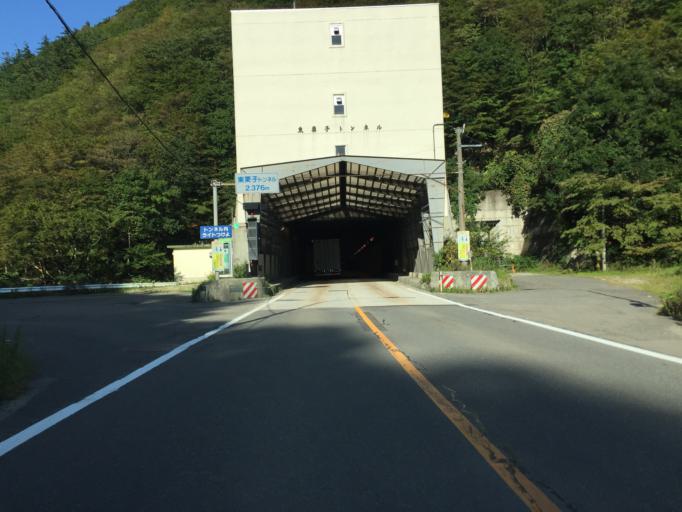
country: JP
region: Yamagata
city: Yonezawa
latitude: 37.8226
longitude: 140.2784
